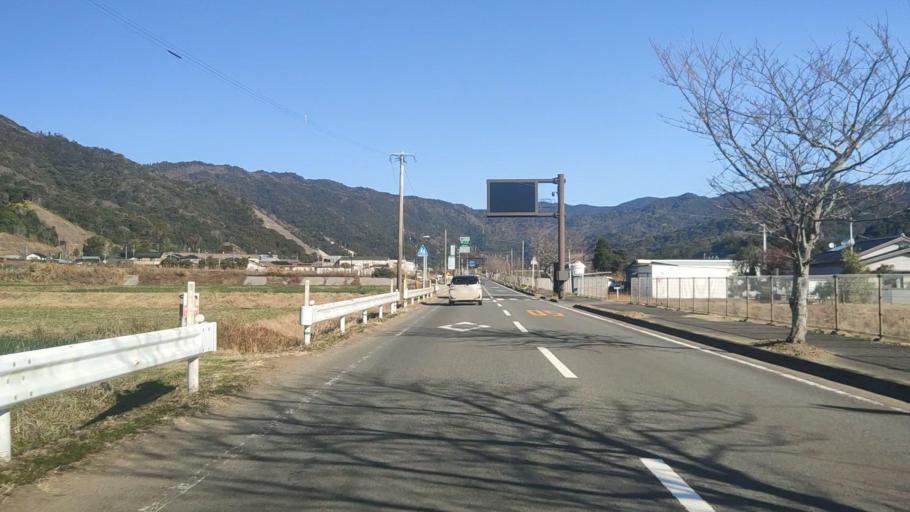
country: JP
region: Miyazaki
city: Nobeoka
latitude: 32.7082
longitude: 131.8193
